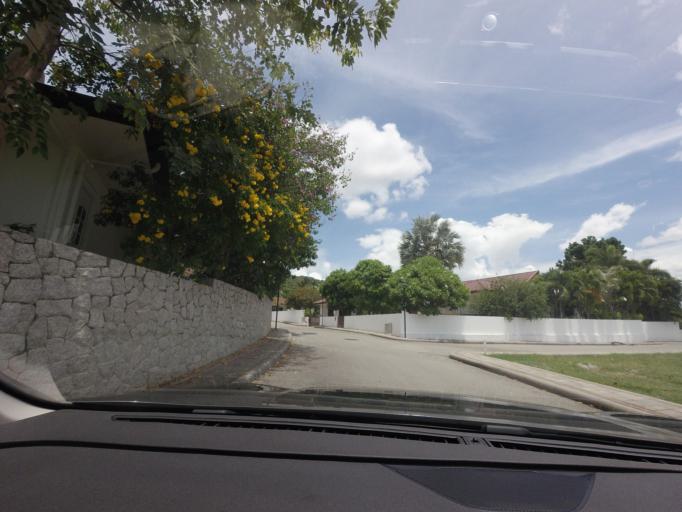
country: TH
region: Prachuap Khiri Khan
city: Hua Hin
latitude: 12.5155
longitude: 99.9577
